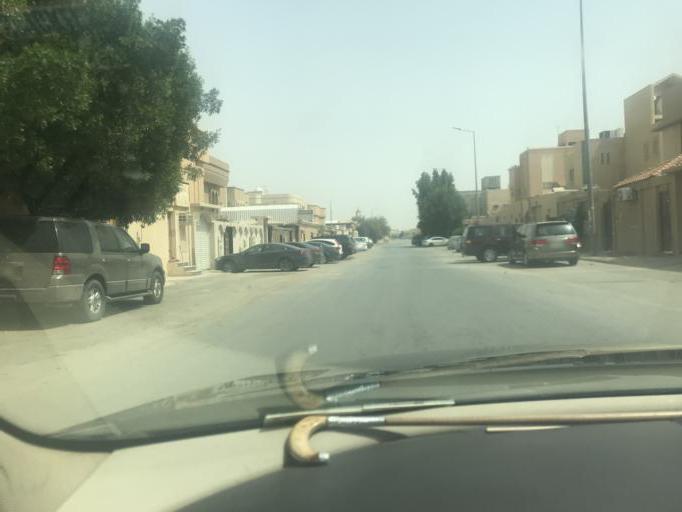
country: SA
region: Ar Riyad
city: Riyadh
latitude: 24.7447
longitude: 46.7713
